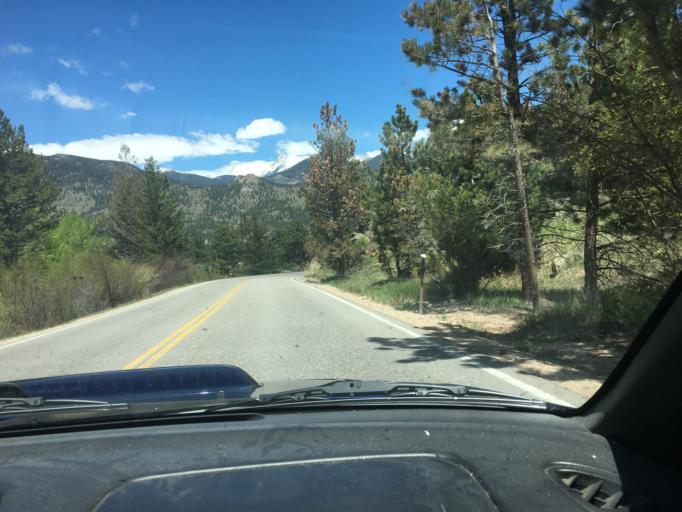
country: US
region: Colorado
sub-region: Larimer County
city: Estes Park
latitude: 40.3523
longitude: -105.5417
